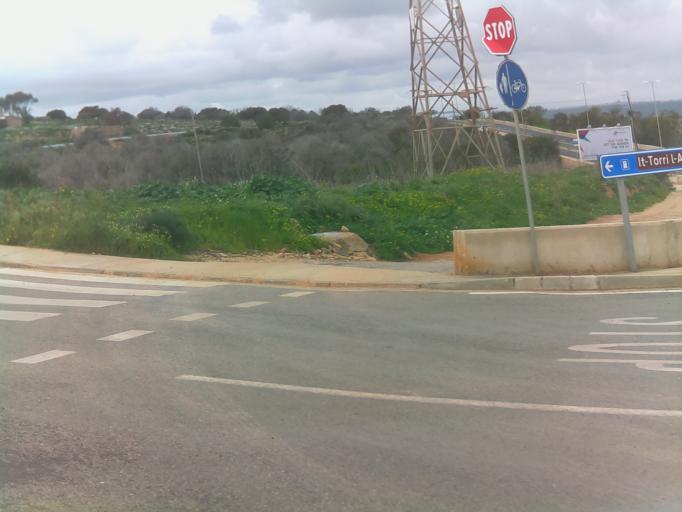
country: MT
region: Il-Mellieha
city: Mellieha
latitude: 35.9766
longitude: 14.3458
